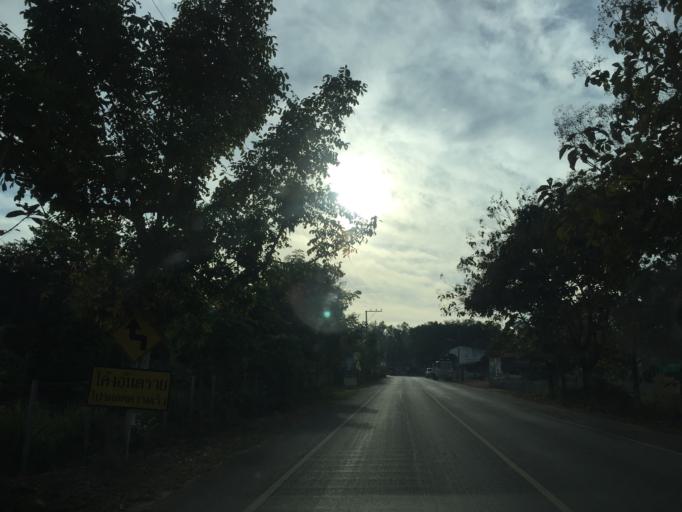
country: TH
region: Lamphun
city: Lamphun
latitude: 18.5123
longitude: 99.0265
